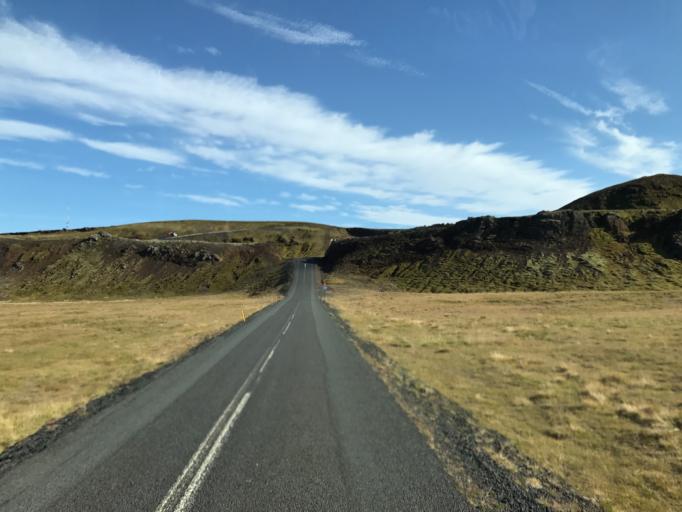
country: IS
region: South
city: Hveragerdi
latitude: 64.1119
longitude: -21.2932
